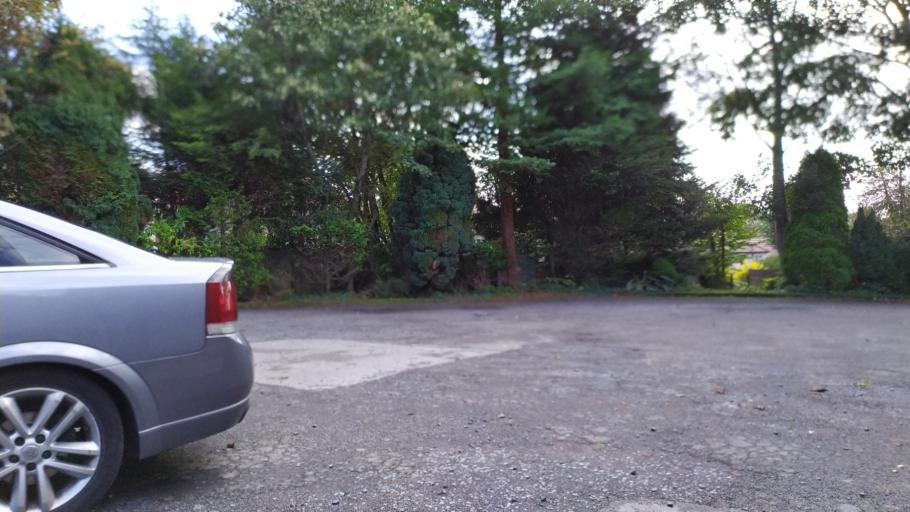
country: GB
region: England
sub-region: City and Borough of Leeds
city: Chapel Allerton
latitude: 53.8285
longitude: -1.5780
